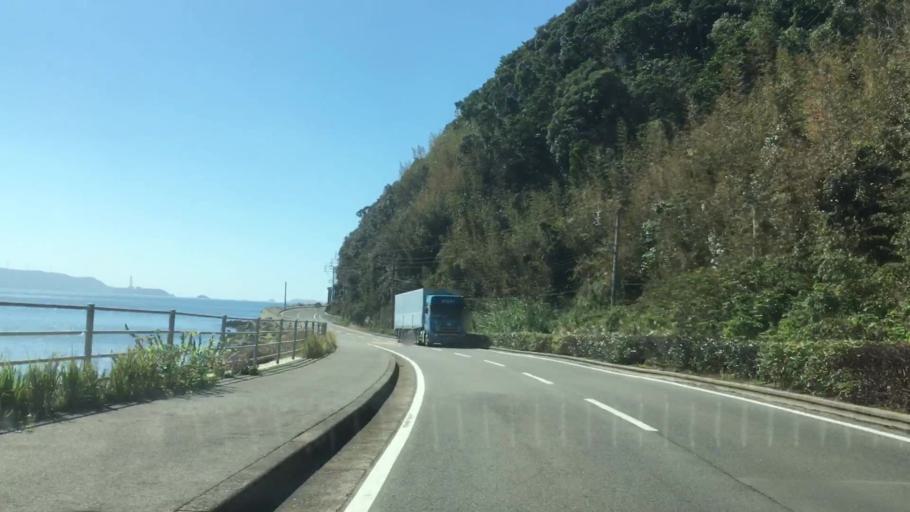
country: JP
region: Nagasaki
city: Sasebo
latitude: 33.0275
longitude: 129.6013
